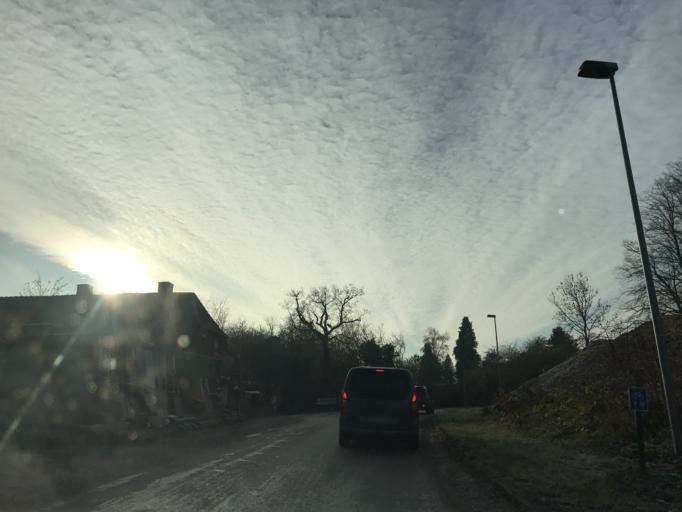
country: DK
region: South Denmark
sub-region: Aabenraa Kommune
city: Lojt Kirkeby
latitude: 55.1403
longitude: 9.4839
